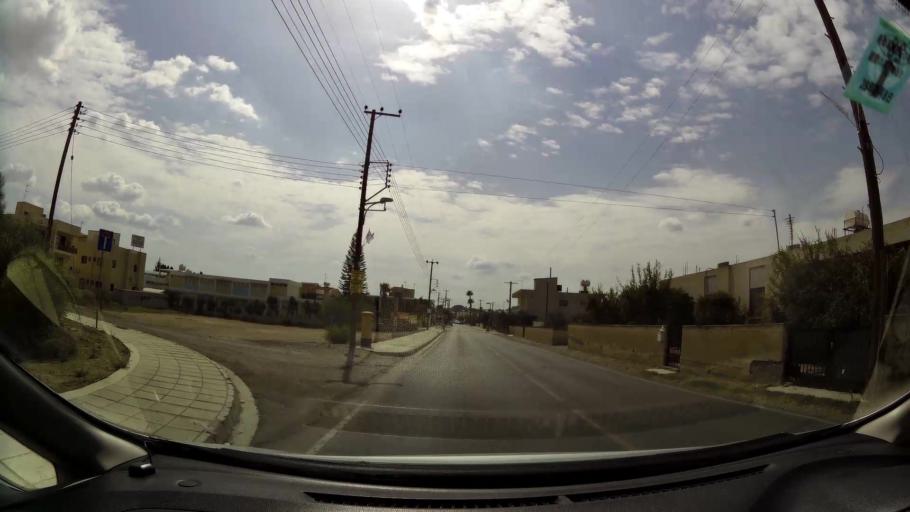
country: CY
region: Lefkosia
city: Tseri
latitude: 35.0695
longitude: 33.3243
